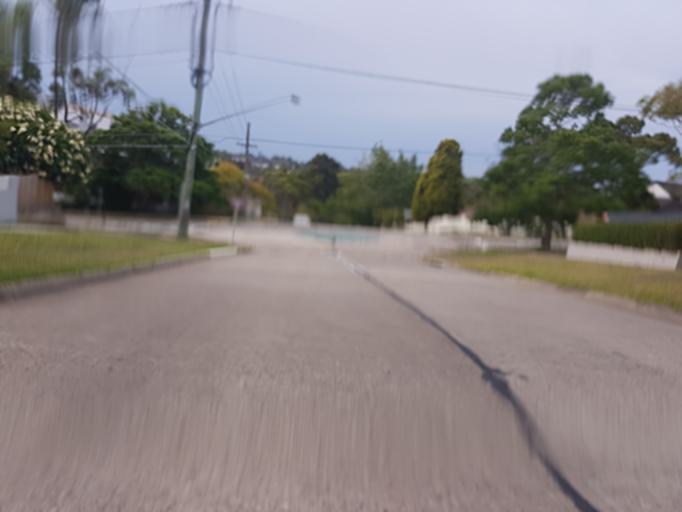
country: AU
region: New South Wales
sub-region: Willoughby
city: Castle Cove
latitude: -33.7905
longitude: 151.2031
